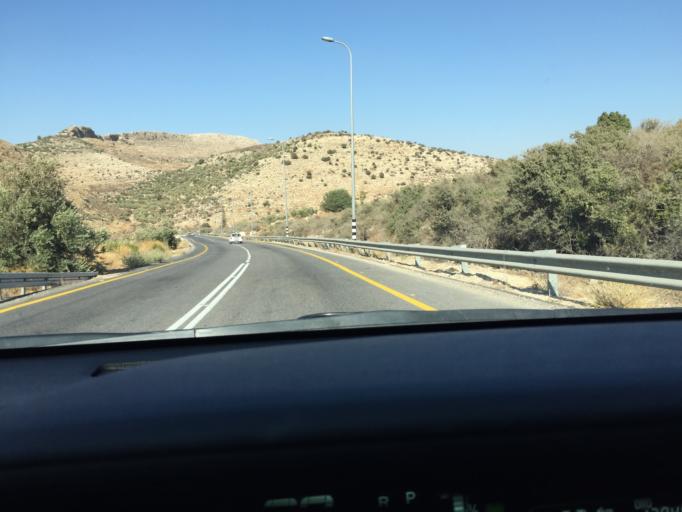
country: PS
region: West Bank
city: Al Lubban al Gharbi
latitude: 32.0477
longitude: 35.0463
